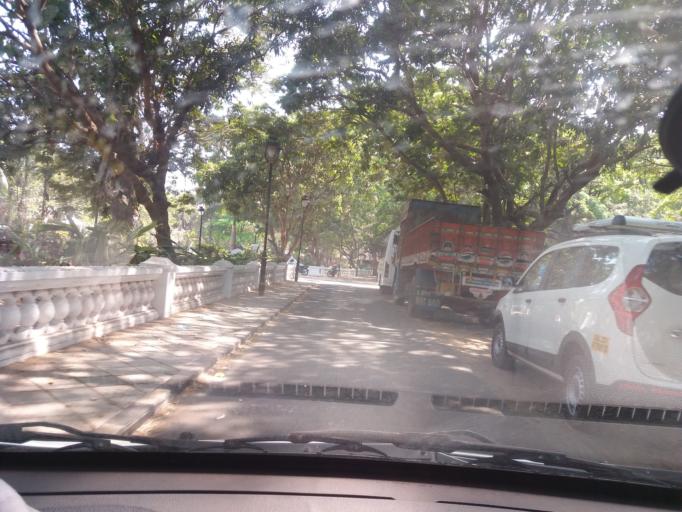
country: IN
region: Goa
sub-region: North Goa
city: Panaji
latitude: 15.4964
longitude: 73.8192
